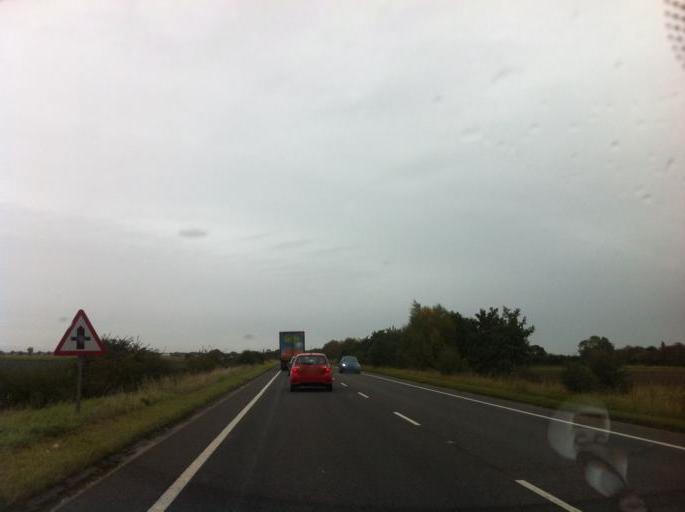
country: GB
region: England
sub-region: Lincolnshire
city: Gosberton
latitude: 52.8715
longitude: -0.0991
